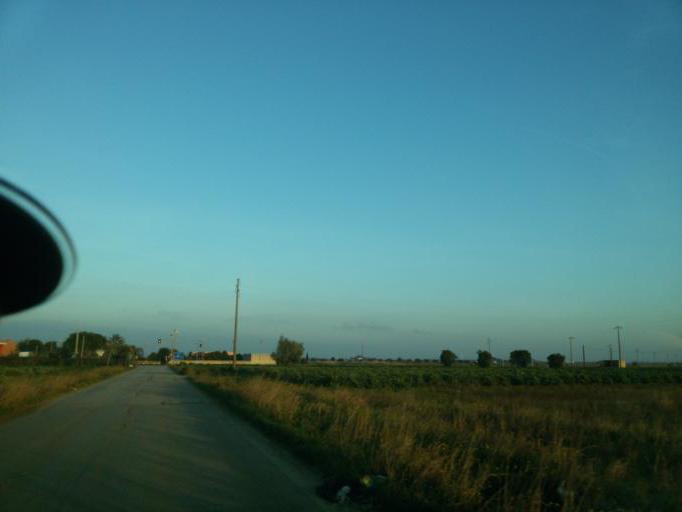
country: IT
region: Apulia
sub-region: Provincia di Brindisi
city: La Rosa
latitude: 40.5912
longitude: 17.9418
